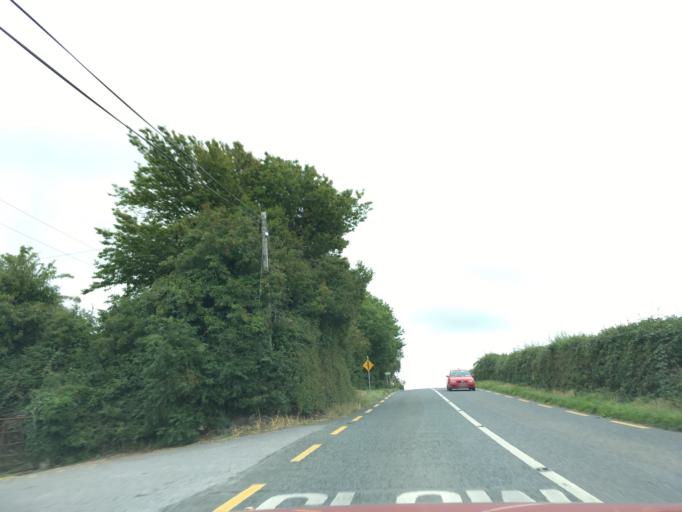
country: IE
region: Munster
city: Fethard
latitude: 52.4195
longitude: -7.7643
